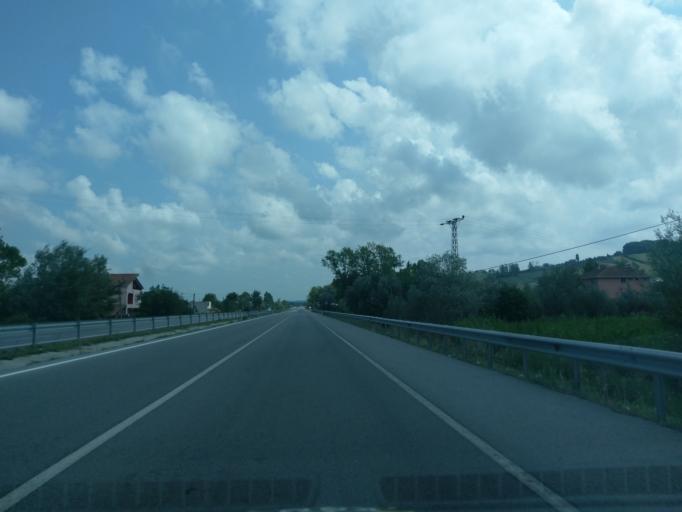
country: TR
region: Samsun
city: Alacam
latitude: 41.6106
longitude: 35.7183
